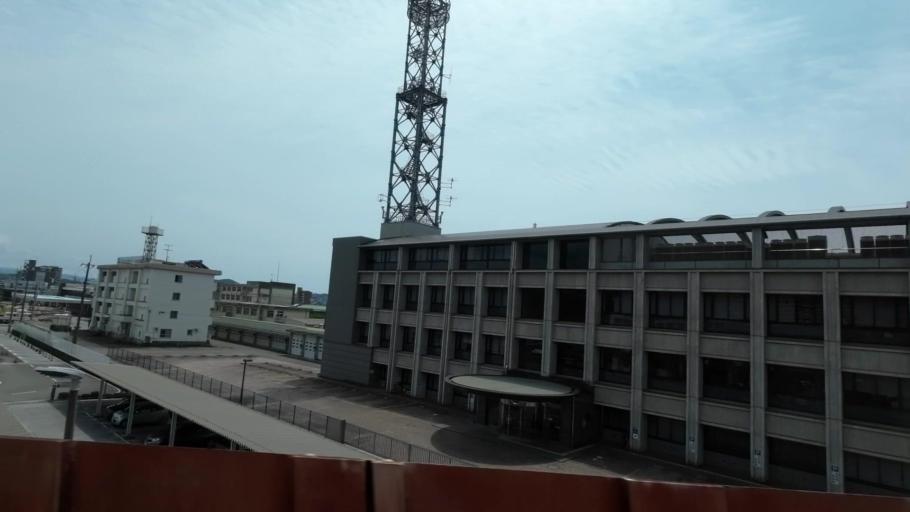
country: JP
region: Kochi
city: Kochi-shi
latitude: 33.5679
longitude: 133.5511
